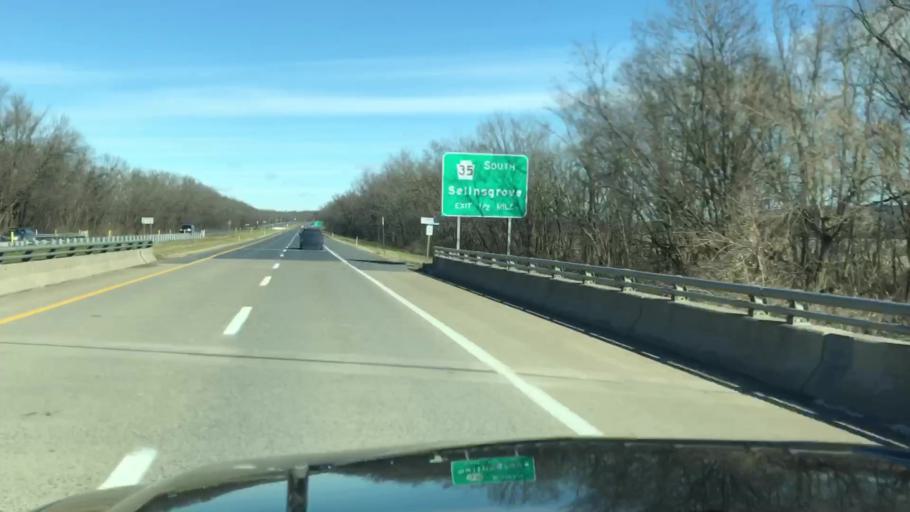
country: US
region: Pennsylvania
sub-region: Snyder County
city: Selinsgrove
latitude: 40.7754
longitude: -76.8664
